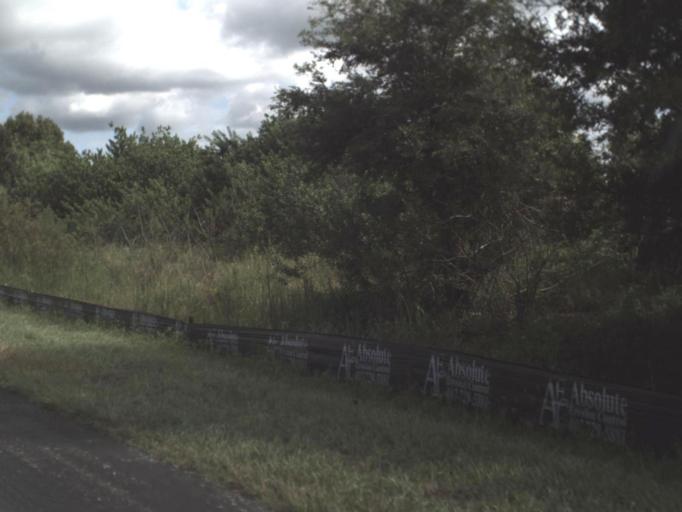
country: US
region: Florida
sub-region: Polk County
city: Combee Settlement
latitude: 28.1098
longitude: -81.9059
